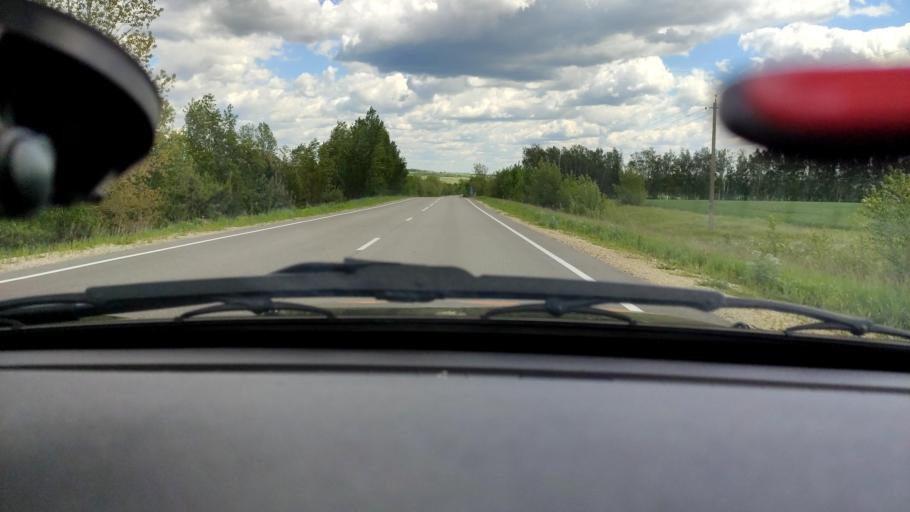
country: RU
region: Belgorod
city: Krasnoye
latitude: 51.0681
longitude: 38.8011
